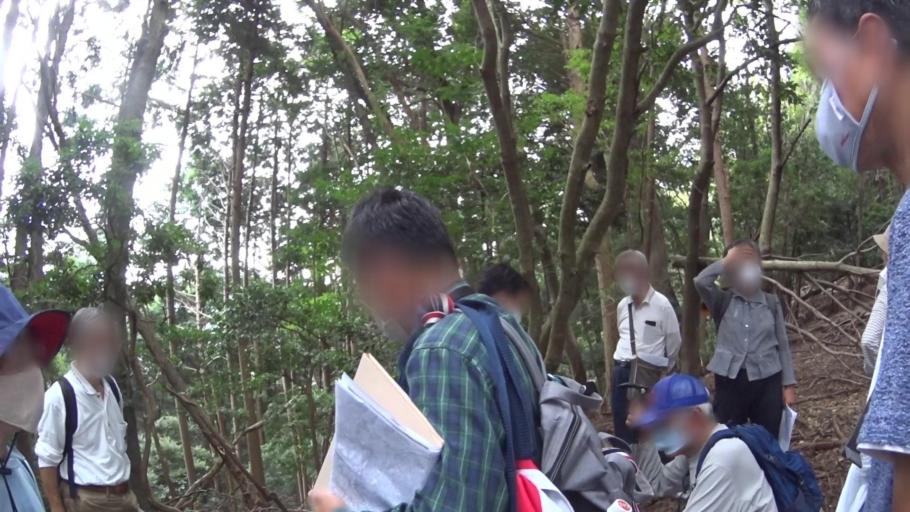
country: JP
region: Osaka
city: Kaizuka
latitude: 34.4916
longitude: 135.3242
